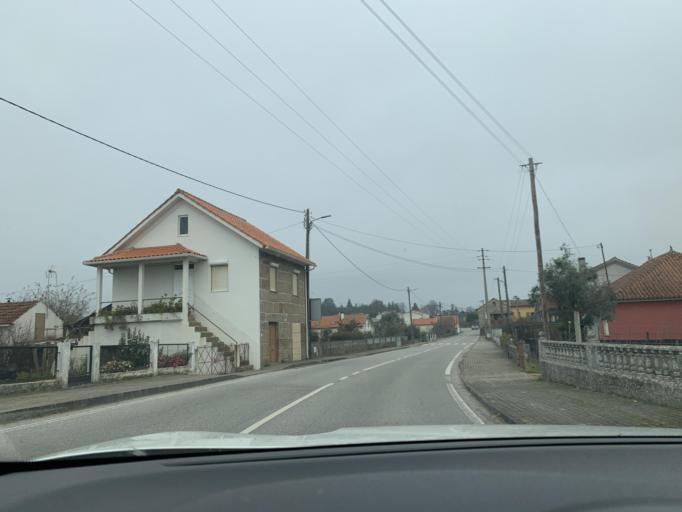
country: PT
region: Viseu
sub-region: Concelho de Tondela
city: Tondela
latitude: 40.4989
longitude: -8.0748
